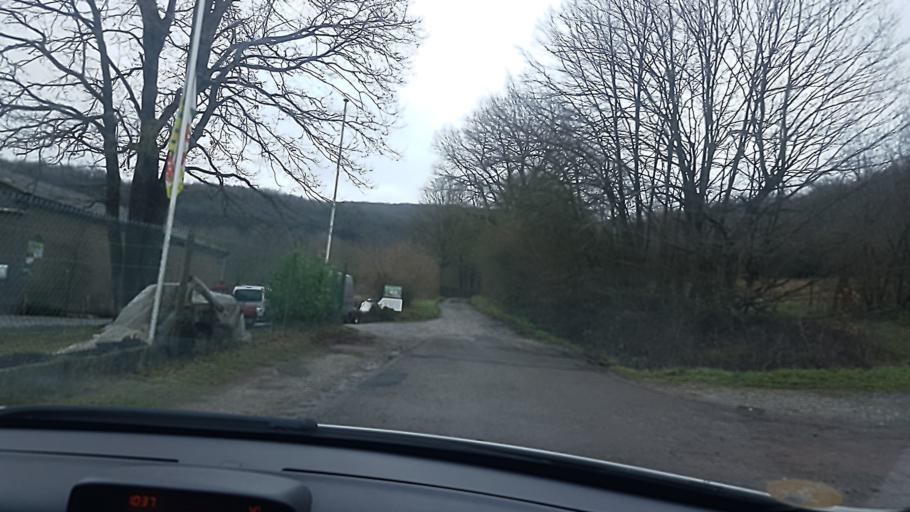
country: FR
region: Champagne-Ardenne
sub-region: Departement des Ardennes
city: Haybes
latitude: 50.0651
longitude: 4.6130
